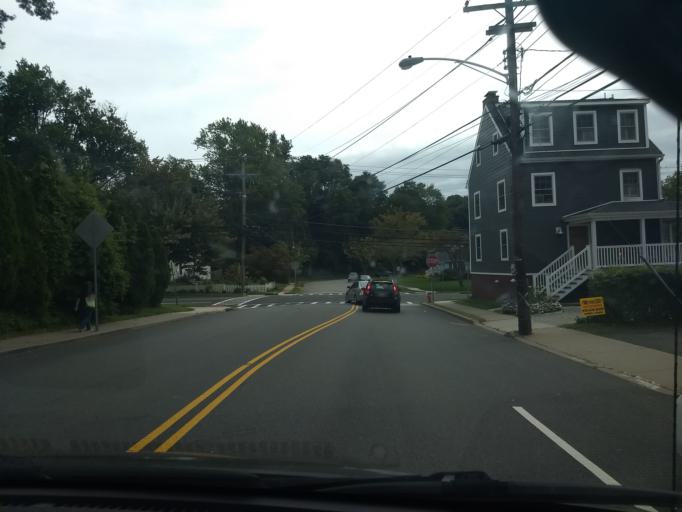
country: US
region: New Jersey
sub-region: Morris County
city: Morristown
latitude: 40.7895
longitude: -74.4779
